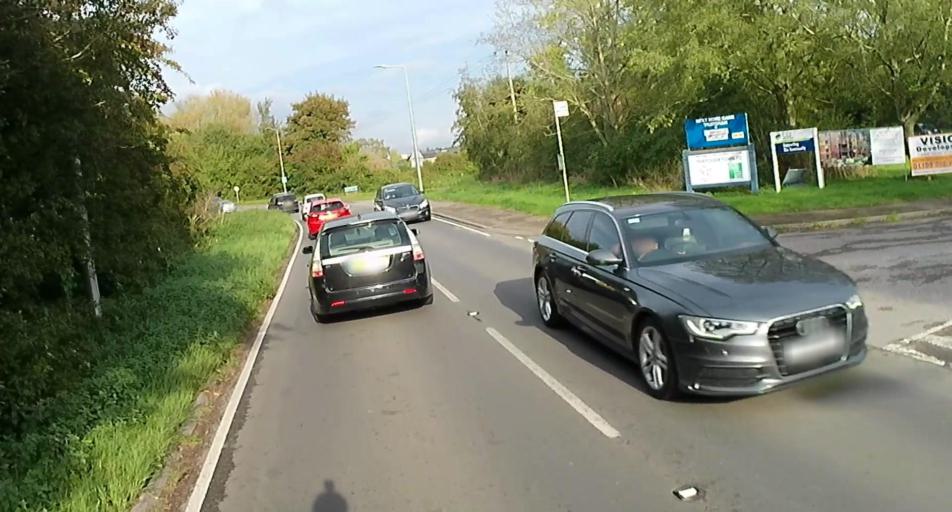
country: GB
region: England
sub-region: West Berkshire
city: Thatcham
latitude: 51.3916
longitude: -1.2444
